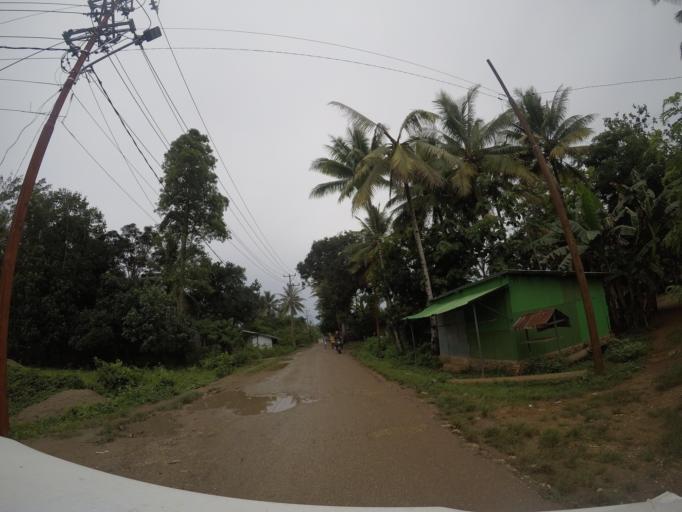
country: TL
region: Lautem
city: Lospalos
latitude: -8.5260
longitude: 126.9977
